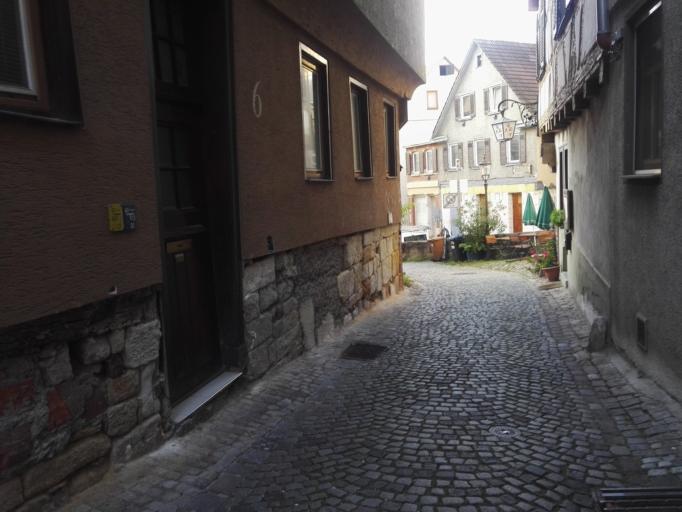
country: DE
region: Baden-Wuerttemberg
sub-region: Regierungsbezirk Stuttgart
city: Esslingen
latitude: 48.7441
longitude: 9.3068
